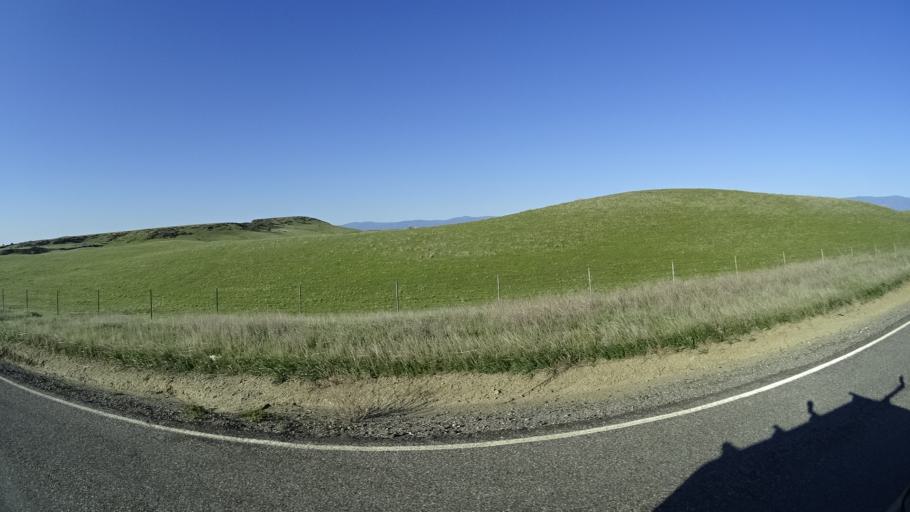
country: US
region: California
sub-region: Glenn County
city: Orland
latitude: 39.8304
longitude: -122.3405
